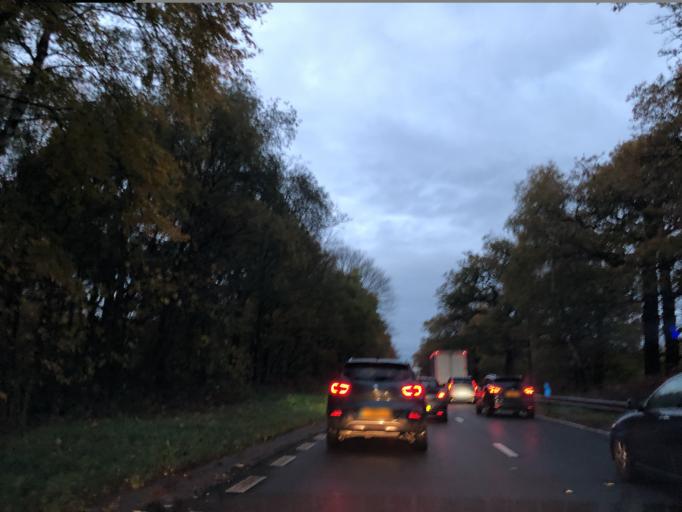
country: GB
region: England
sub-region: Solihull
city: Chelmsley Wood
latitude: 52.4710
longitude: -1.7061
